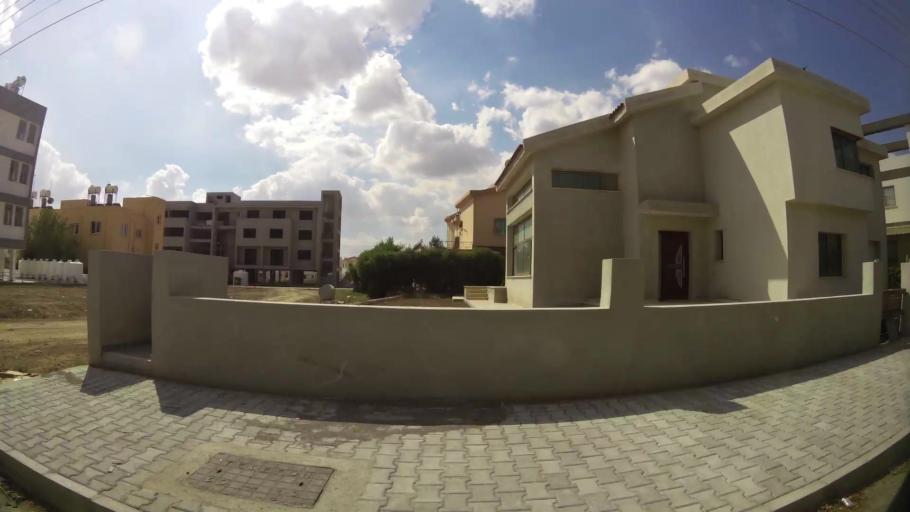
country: CY
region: Lefkosia
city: Nicosia
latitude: 35.2207
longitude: 33.2961
